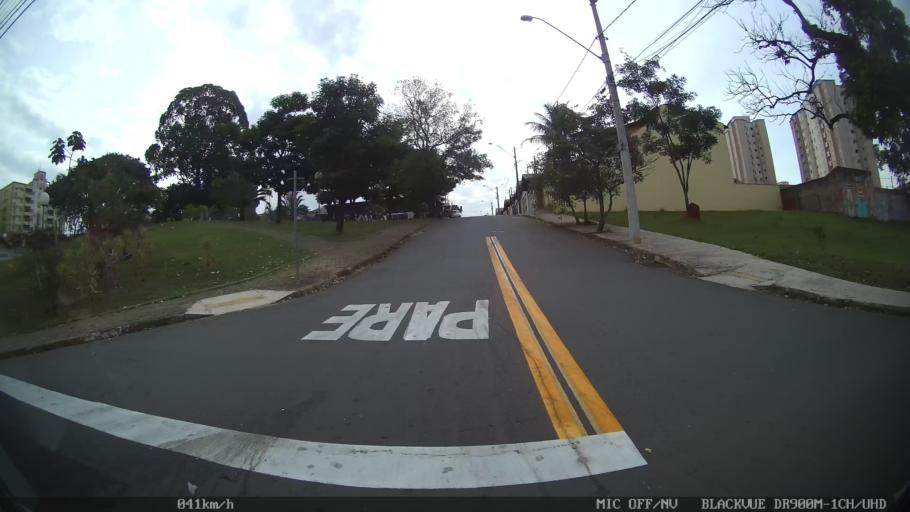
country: BR
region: Sao Paulo
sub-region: Piracicaba
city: Piracicaba
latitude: -22.7457
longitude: -47.6328
